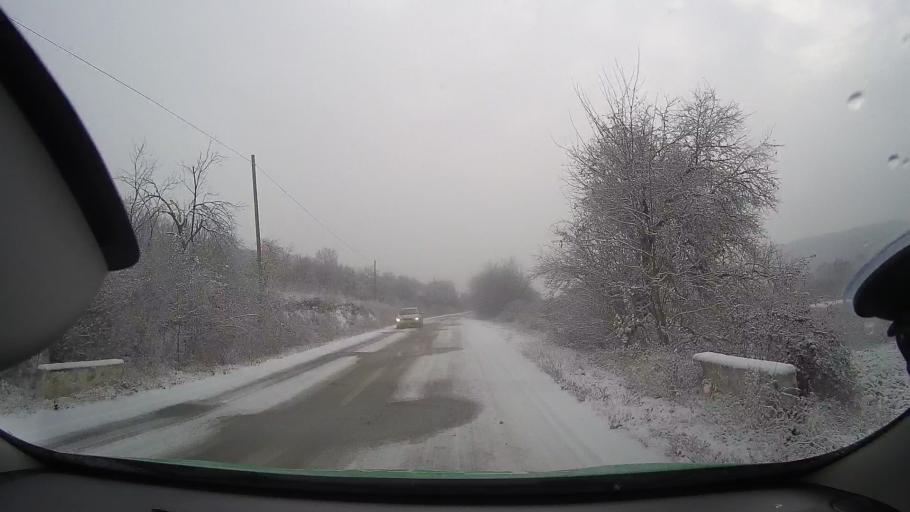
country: RO
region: Alba
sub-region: Municipiul Aiud
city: Aiudul de Sus
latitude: 46.3358
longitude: 23.6713
